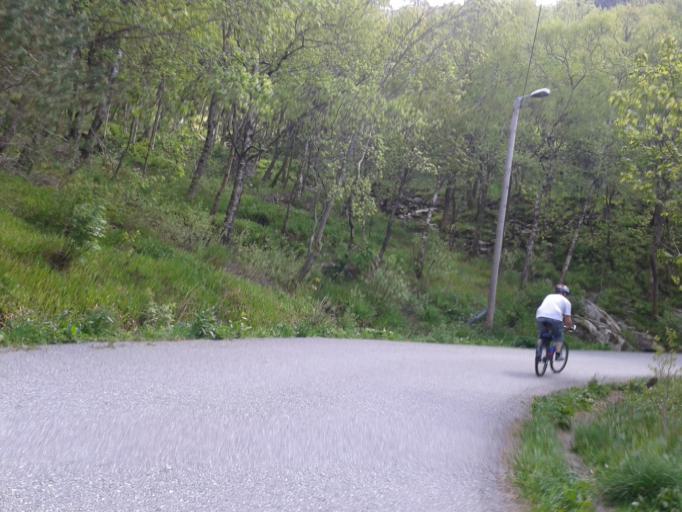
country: NO
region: Hordaland
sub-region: Bergen
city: Bergen
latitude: 60.4192
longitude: 5.3206
